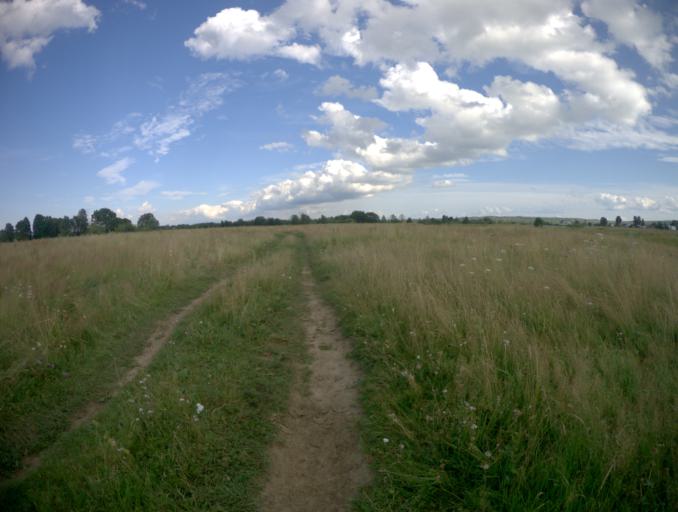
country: RU
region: Vladimir
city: Raduzhnyy
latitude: 56.0412
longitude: 40.3024
